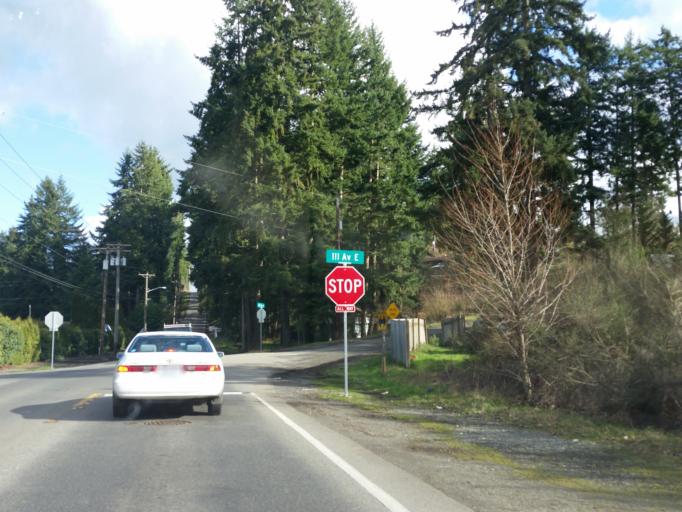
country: US
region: Washington
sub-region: Pierce County
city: South Hill
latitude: 47.1400
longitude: -122.2811
